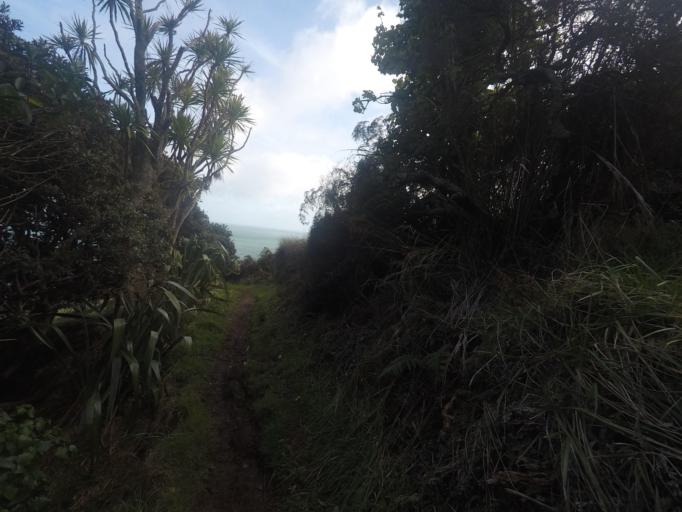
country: NZ
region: Auckland
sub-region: Auckland
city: Muriwai Beach
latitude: -36.8766
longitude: 174.4322
